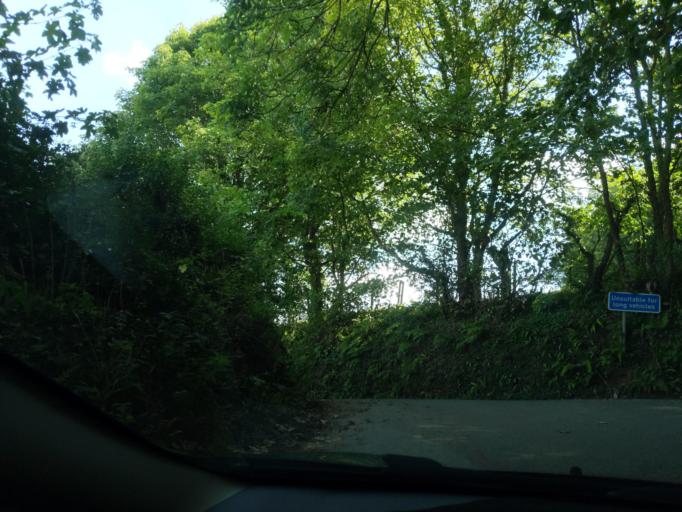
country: GB
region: England
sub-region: Cornwall
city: Torpoint
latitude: 50.3577
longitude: -4.2351
